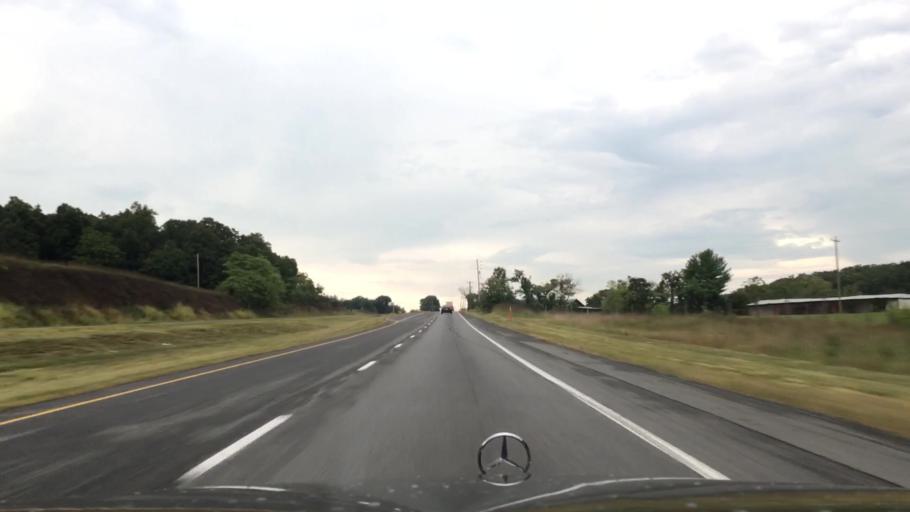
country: US
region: Virginia
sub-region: Frederick County
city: Shawnee Land
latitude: 39.3527
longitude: -78.3069
